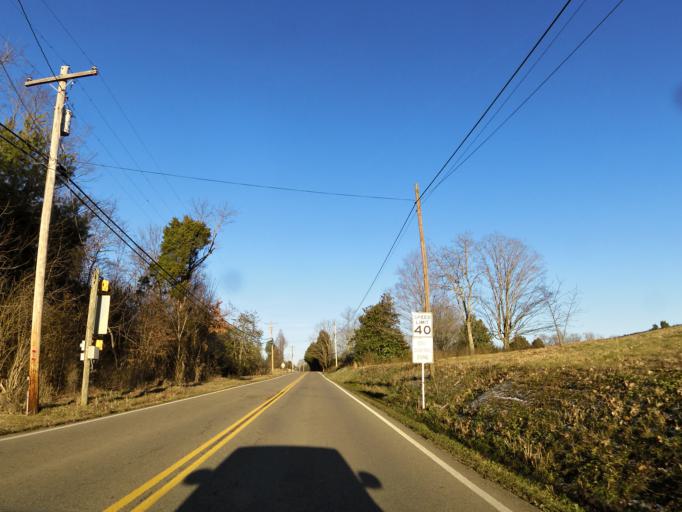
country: US
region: Tennessee
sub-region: Knox County
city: Farragut
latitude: 35.9543
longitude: -84.1191
